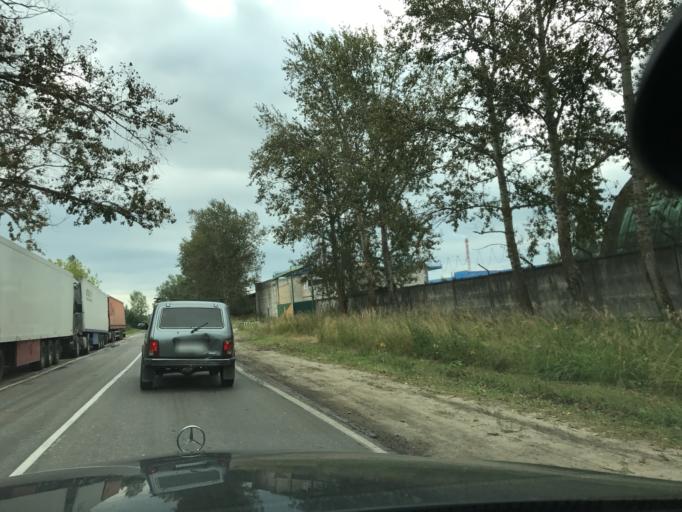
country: RU
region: Vladimir
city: Gorokhovets
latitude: 56.1941
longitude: 42.7346
